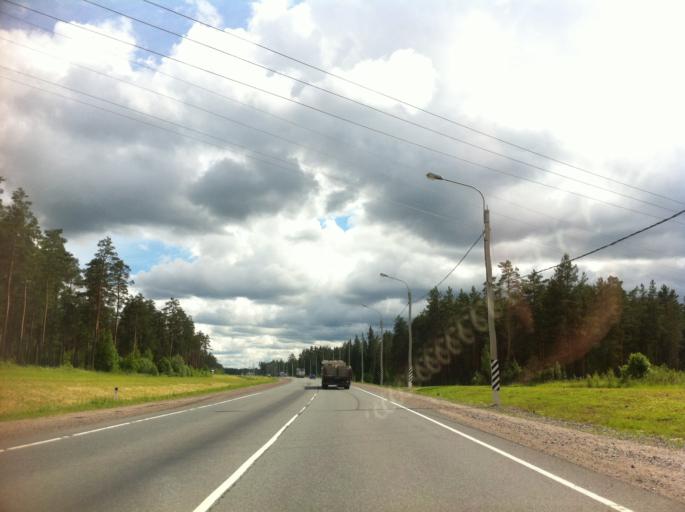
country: RU
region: Leningrad
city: Luga
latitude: 58.7208
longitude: 29.8776
